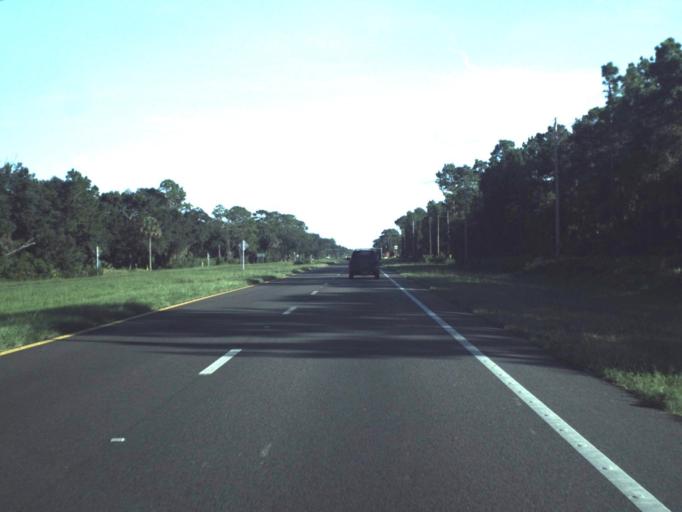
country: US
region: Florida
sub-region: Citrus County
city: Crystal River
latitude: 28.9566
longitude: -82.6289
